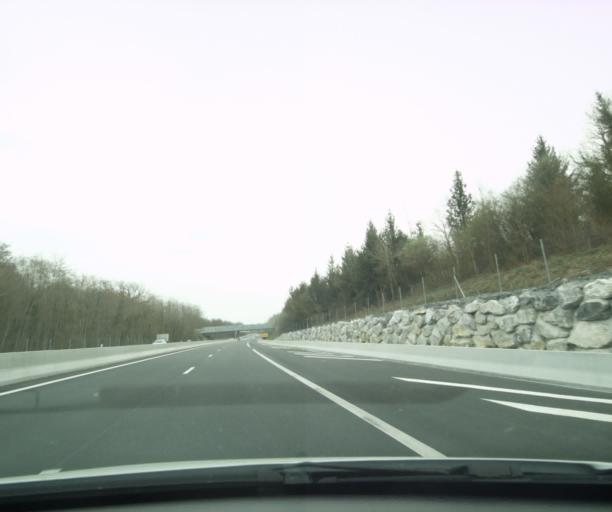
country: FR
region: Aquitaine
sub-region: Departement des Pyrenees-Atlantiques
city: Mouguerre
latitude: 43.4551
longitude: -1.4025
